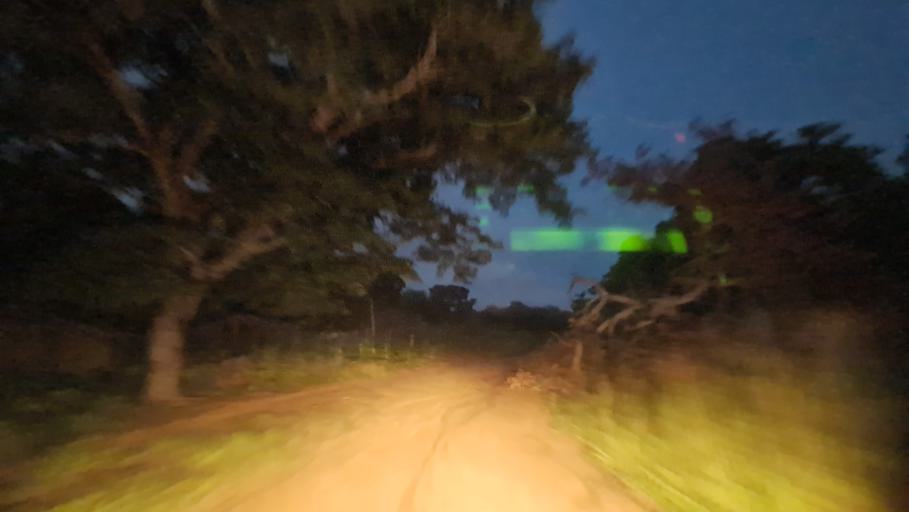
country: MZ
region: Nampula
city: Nampula
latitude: -14.6753
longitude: 39.8314
